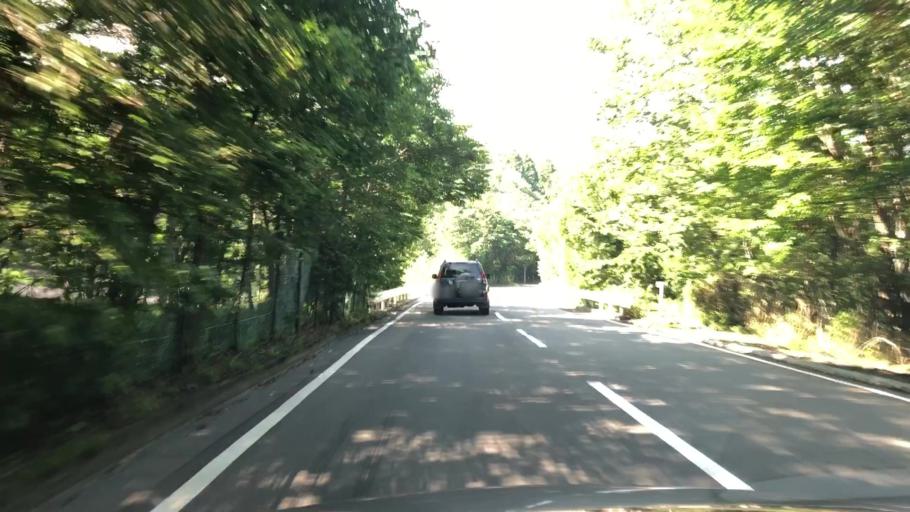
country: JP
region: Shizuoka
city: Gotemba
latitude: 35.3166
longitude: 138.7873
